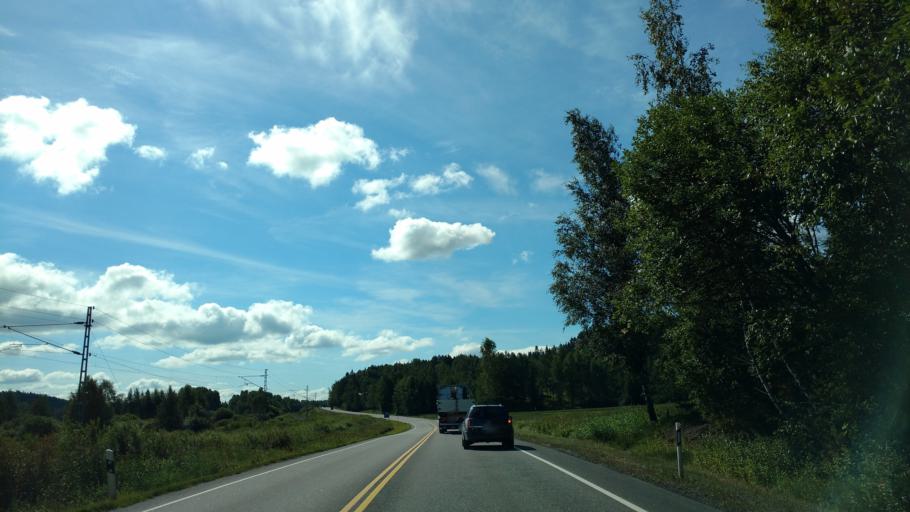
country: FI
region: Varsinais-Suomi
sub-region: Salo
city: Salo
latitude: 60.2981
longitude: 23.1095
